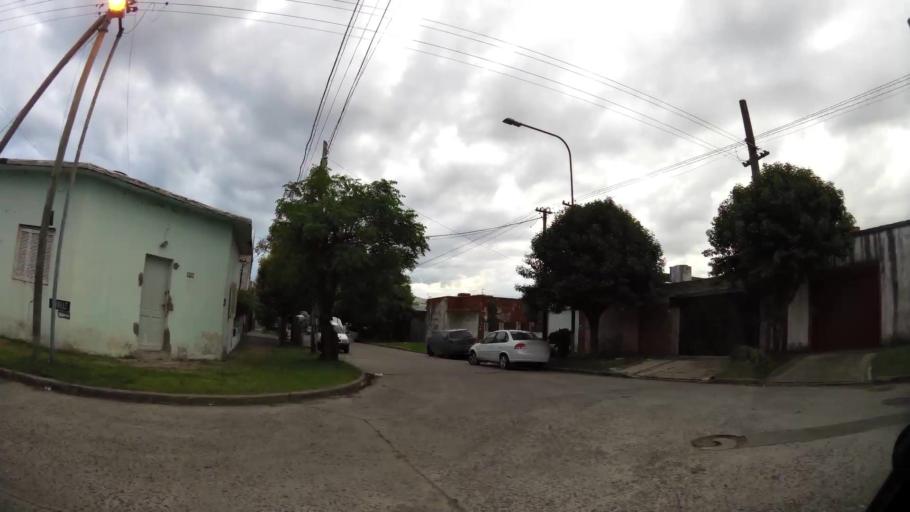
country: AR
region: Buenos Aires
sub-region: Partido de Quilmes
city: Quilmes
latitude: -34.7454
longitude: -58.2387
